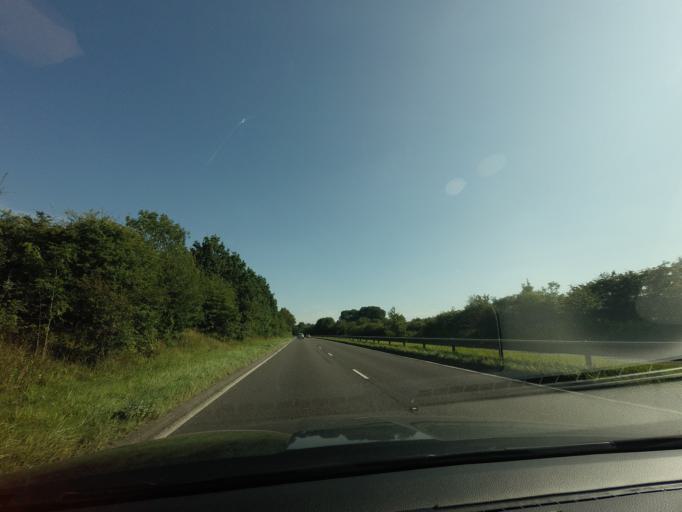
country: GB
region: England
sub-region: Derbyshire
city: Chesterfield
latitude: 53.2172
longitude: -1.3955
